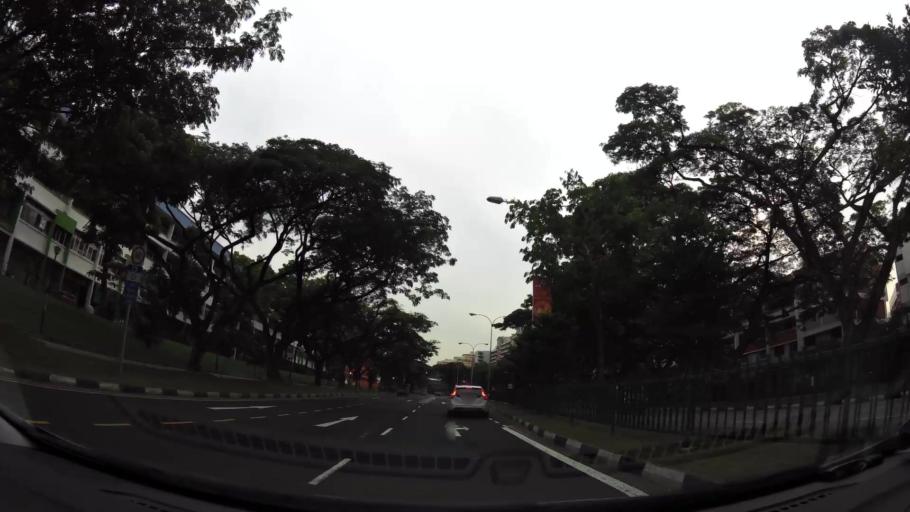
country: SG
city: Singapore
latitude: 1.3530
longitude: 103.8910
